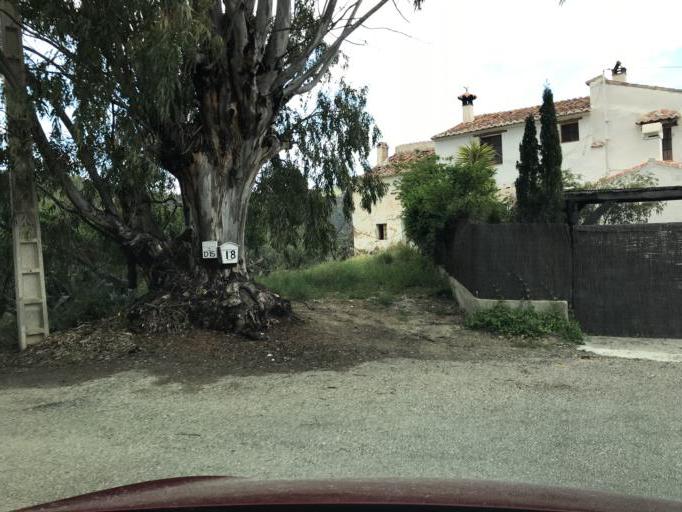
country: ES
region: Andalusia
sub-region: Provincia de Malaga
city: Comares
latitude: 36.8733
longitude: -4.2676
